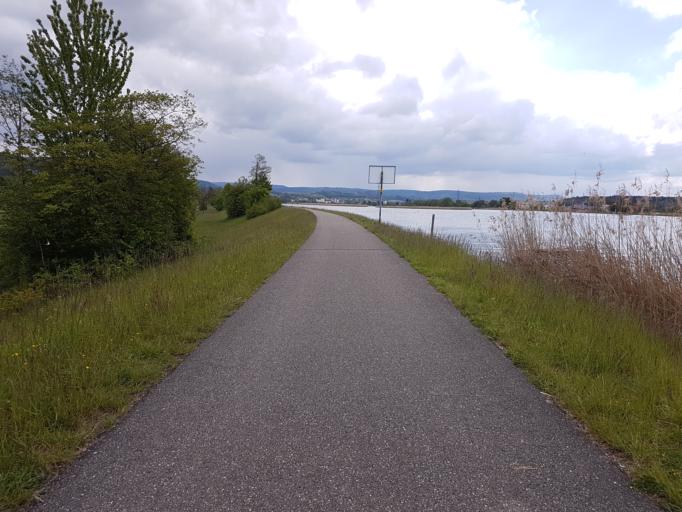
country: CH
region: Aargau
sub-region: Bezirk Zurzach
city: Koblenz
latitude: 47.5896
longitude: 8.2320
